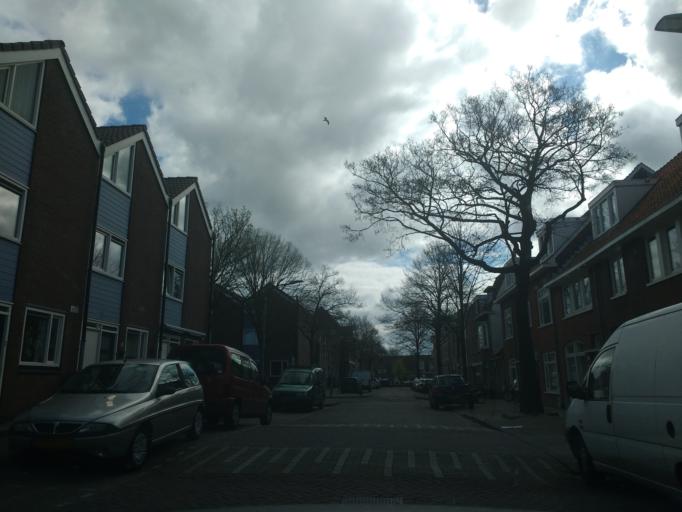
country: NL
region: North Holland
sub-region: Gemeente Haarlem
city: Haarlem
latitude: 52.3730
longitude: 4.6395
